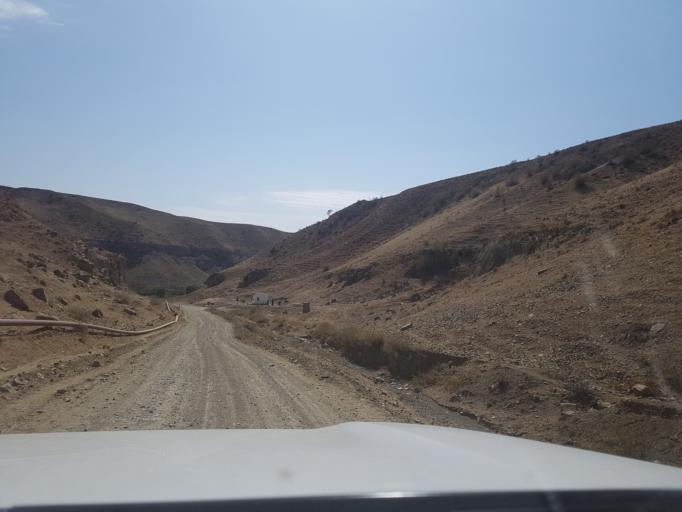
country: TM
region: Ahal
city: Baharly
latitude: 38.2380
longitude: 56.8927
